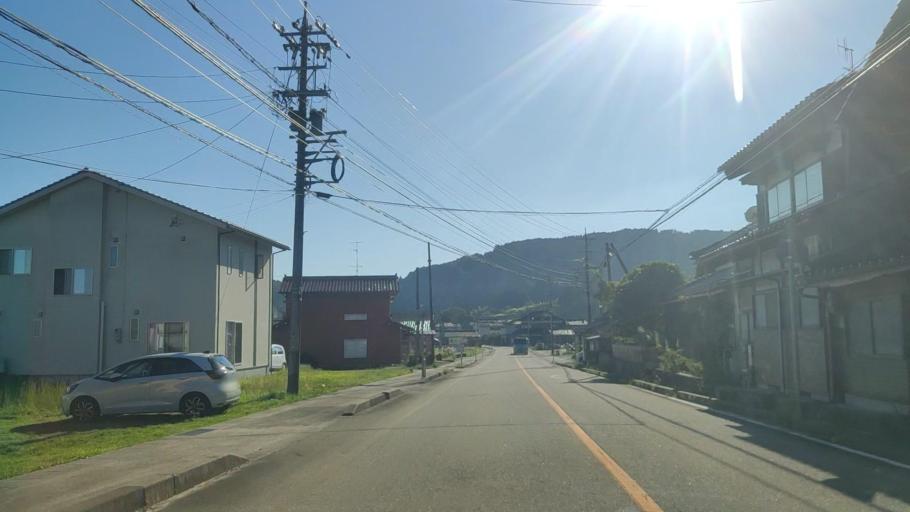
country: JP
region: Ishikawa
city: Nanao
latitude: 37.1474
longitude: 136.8748
